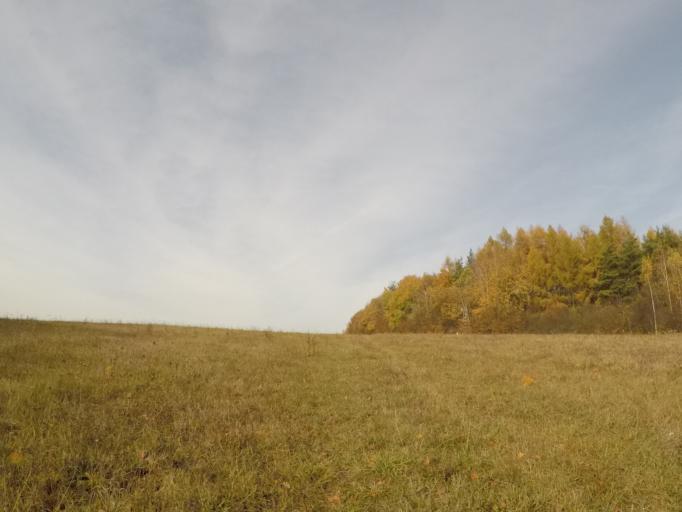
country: SK
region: Presovsky
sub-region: Okres Presov
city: Presov
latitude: 48.9219
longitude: 21.2239
